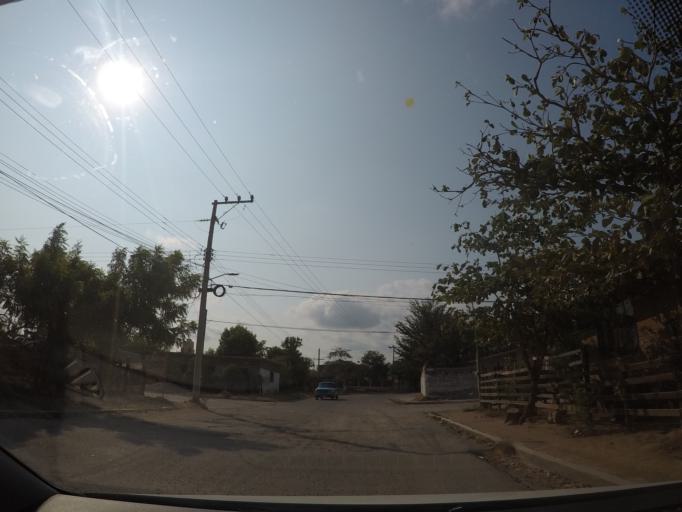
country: MX
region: Oaxaca
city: San Jeronimo Ixtepec
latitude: 16.5520
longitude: -95.1020
